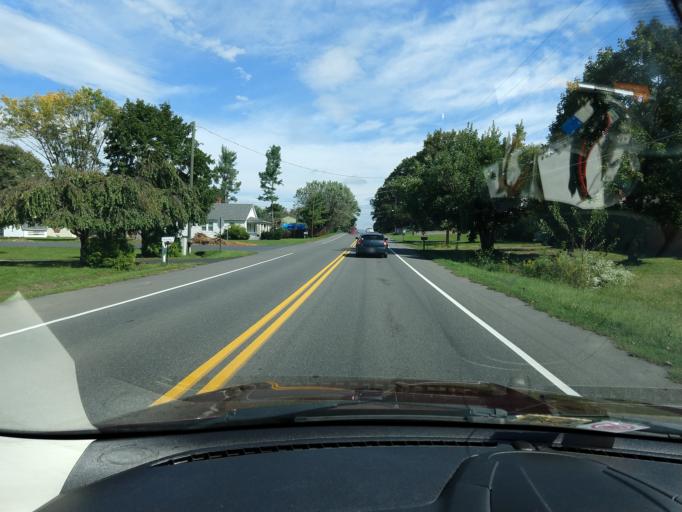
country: US
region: Virginia
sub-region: Rockingham County
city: Grottoes
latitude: 38.2597
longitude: -78.8206
